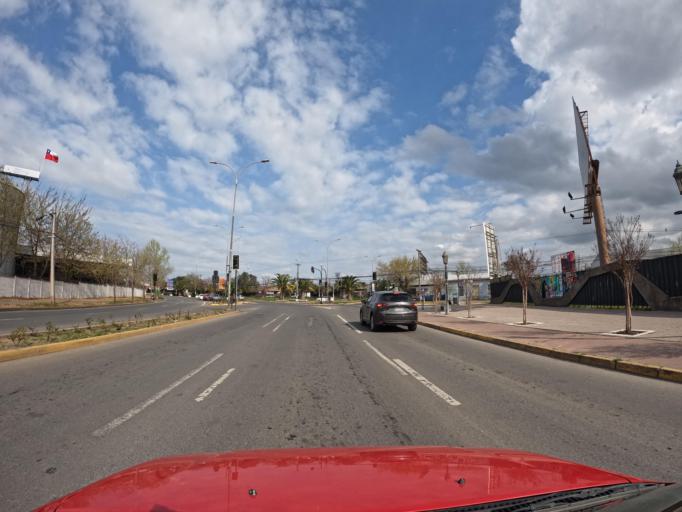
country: CL
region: Maule
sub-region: Provincia de Talca
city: Talca
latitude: -35.4305
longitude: -71.6402
